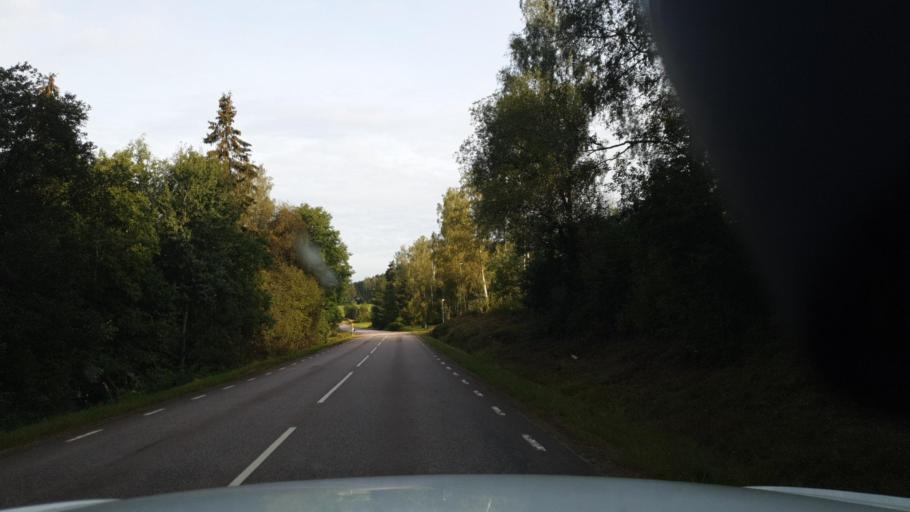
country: SE
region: Vaermland
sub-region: Arvika Kommun
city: Arvika
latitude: 59.7979
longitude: 12.6070
